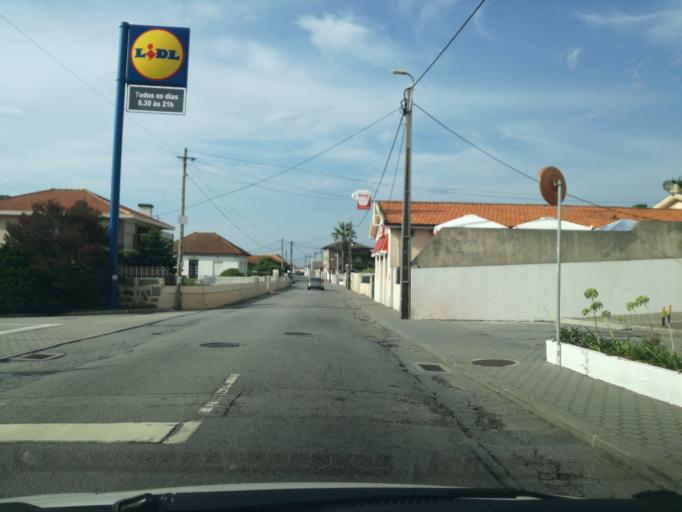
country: PT
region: Porto
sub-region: Vila Nova de Gaia
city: Azenha
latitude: 41.0713
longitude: -8.6254
